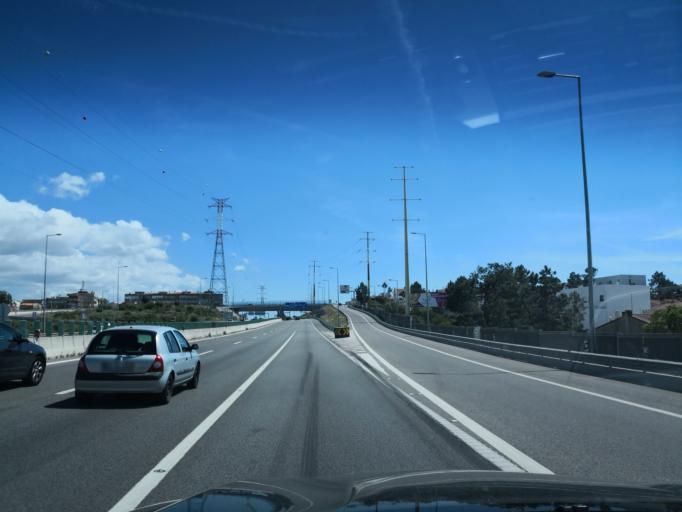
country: PT
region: Setubal
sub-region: Almada
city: Charneca
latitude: 38.6338
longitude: -9.1958
